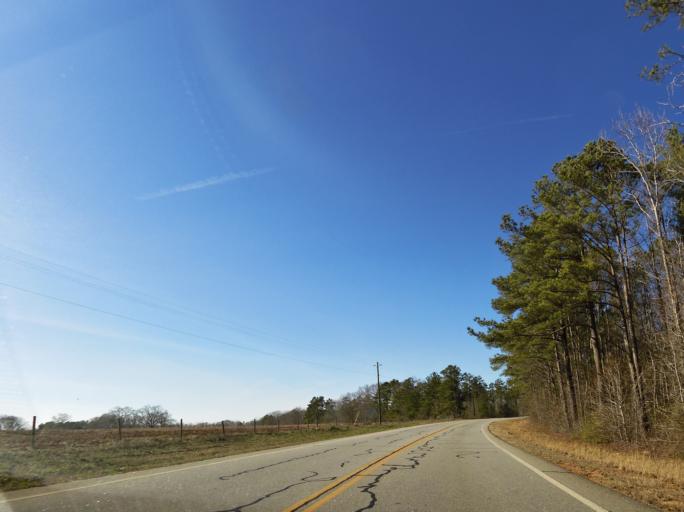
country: US
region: Georgia
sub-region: Lamar County
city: Barnesville
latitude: 32.9068
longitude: -84.1197
